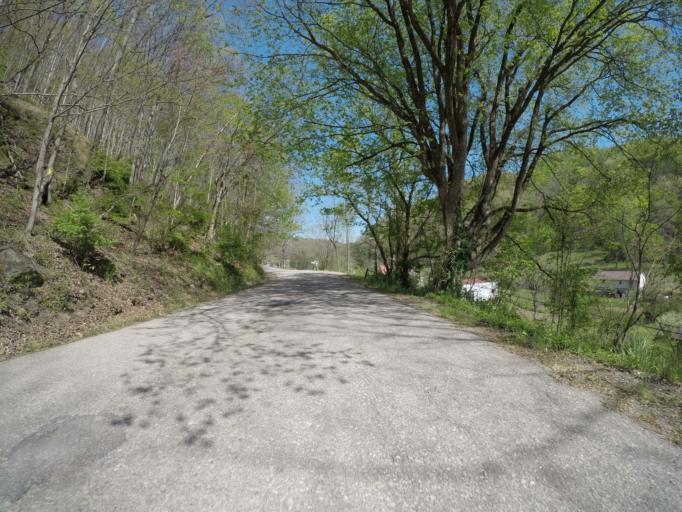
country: US
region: West Virginia
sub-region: Kanawha County
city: Charleston
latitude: 38.4140
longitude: -81.6192
